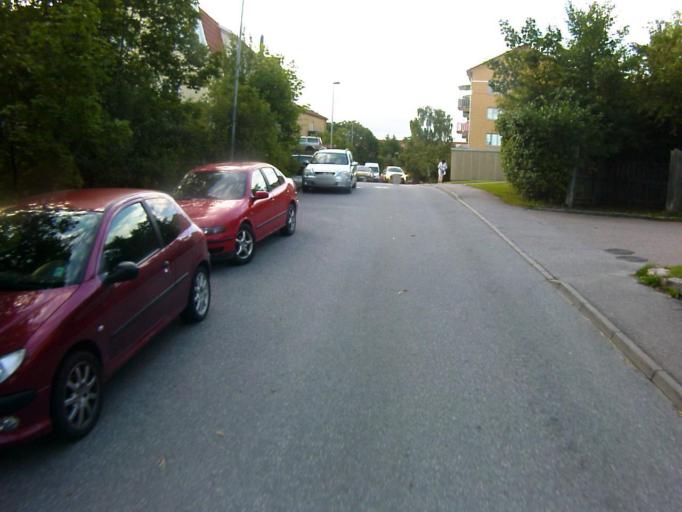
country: SE
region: Soedermanland
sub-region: Eskilstuna Kommun
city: Eskilstuna
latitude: 59.3752
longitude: 16.5344
